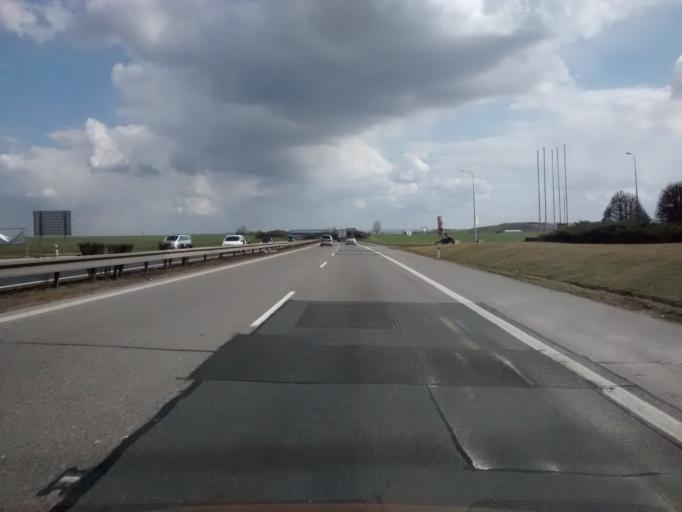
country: CZ
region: Central Bohemia
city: Zdiby
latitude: 50.1699
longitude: 14.4605
